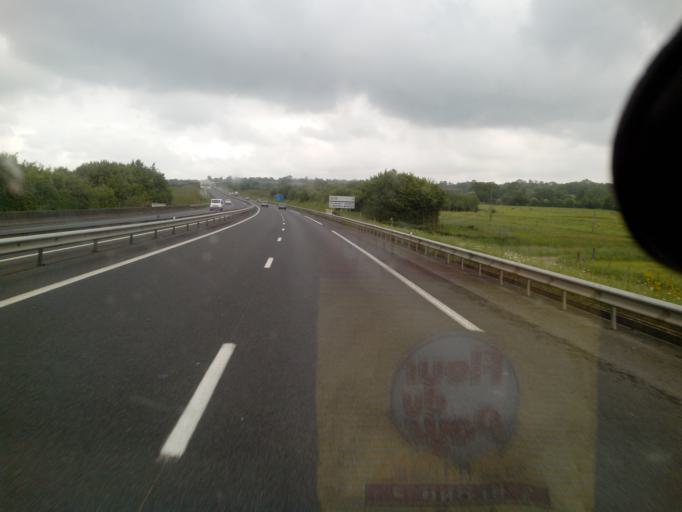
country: FR
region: Lower Normandy
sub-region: Departement de la Manche
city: Saint-Amand
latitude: 48.9849
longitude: -0.9373
